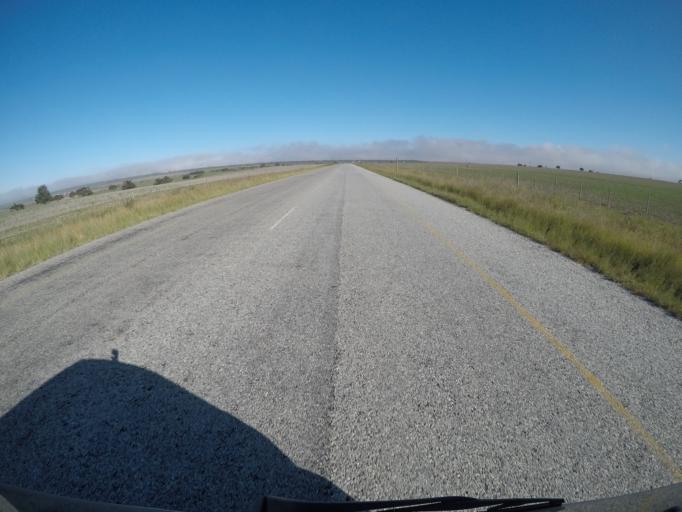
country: ZA
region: Western Cape
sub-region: Eden District Municipality
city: Mossel Bay
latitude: -34.1756
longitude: 22.0157
